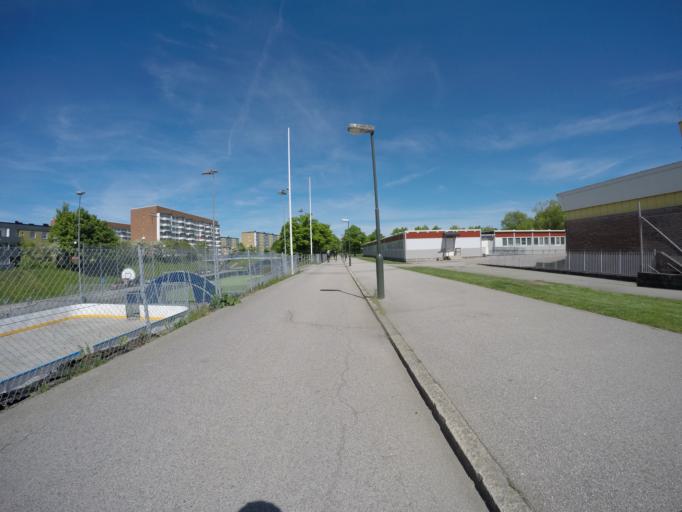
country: SE
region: Skane
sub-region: Malmo
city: Malmoe
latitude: 55.5738
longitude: 12.9767
